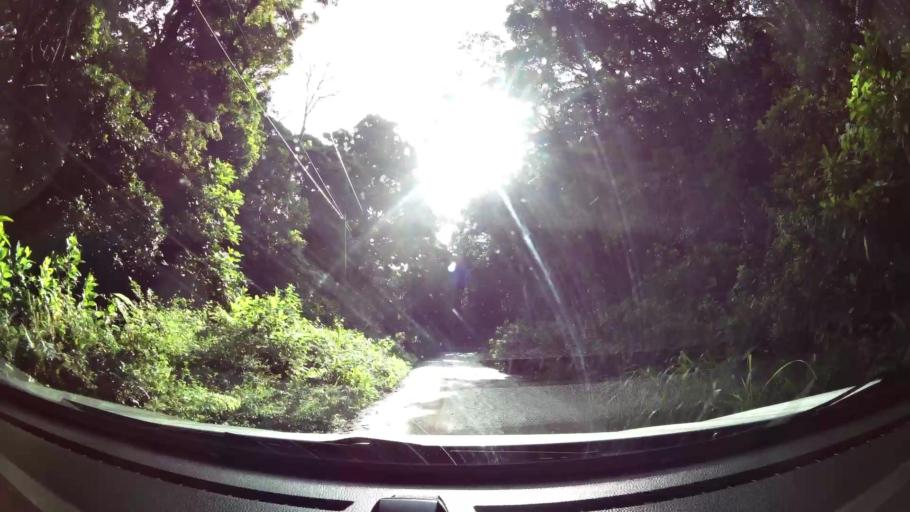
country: CR
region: Guanacaste
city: Juntas
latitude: 10.3016
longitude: -84.8026
